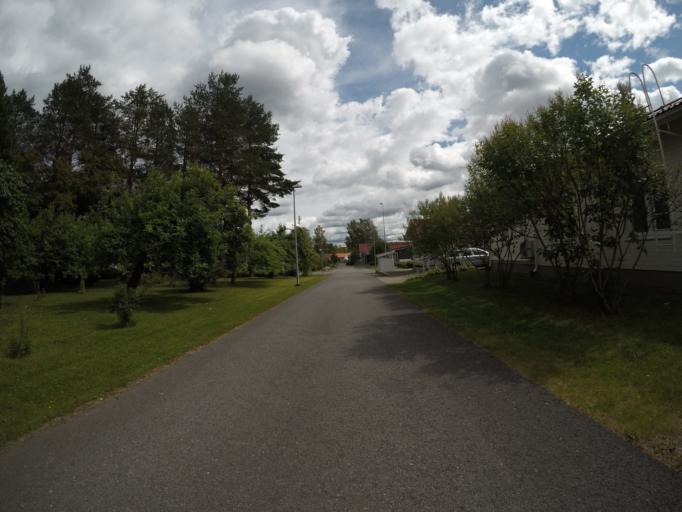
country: FI
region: Haeme
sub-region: Haemeenlinna
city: Haemeenlinna
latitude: 60.9760
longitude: 24.4310
